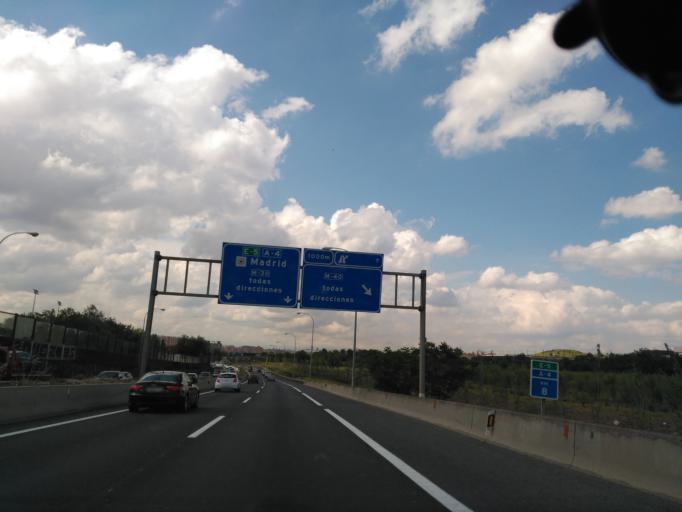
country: ES
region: Madrid
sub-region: Provincia de Madrid
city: Villaverde
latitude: 40.3498
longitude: -3.6744
